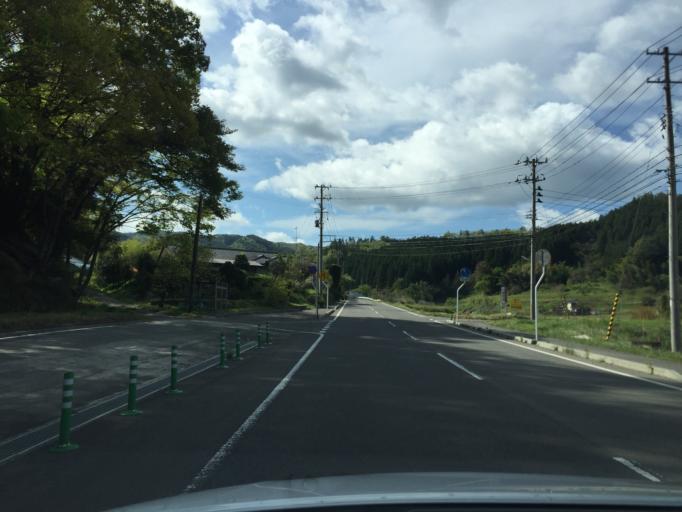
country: JP
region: Fukushima
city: Fukushima-shi
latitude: 37.6498
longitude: 140.6128
